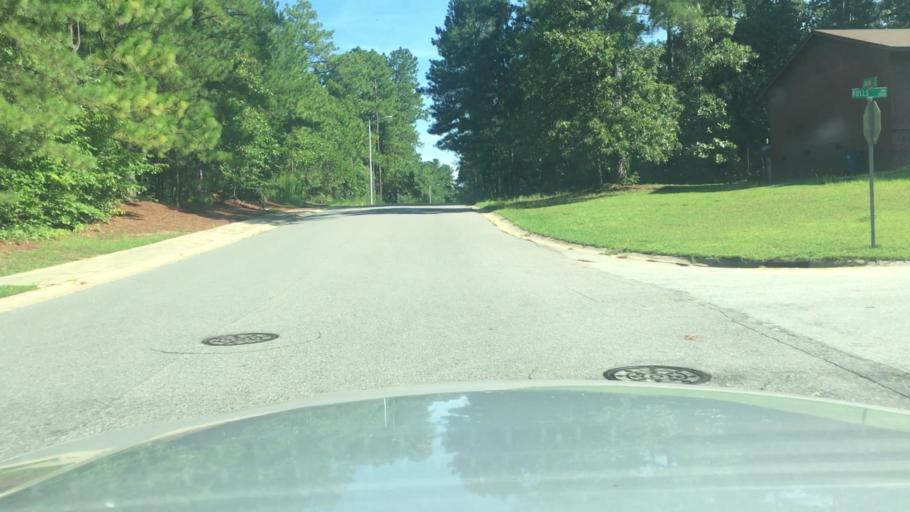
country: US
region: North Carolina
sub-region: Cumberland County
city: Fayetteville
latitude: 35.1098
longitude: -78.9106
